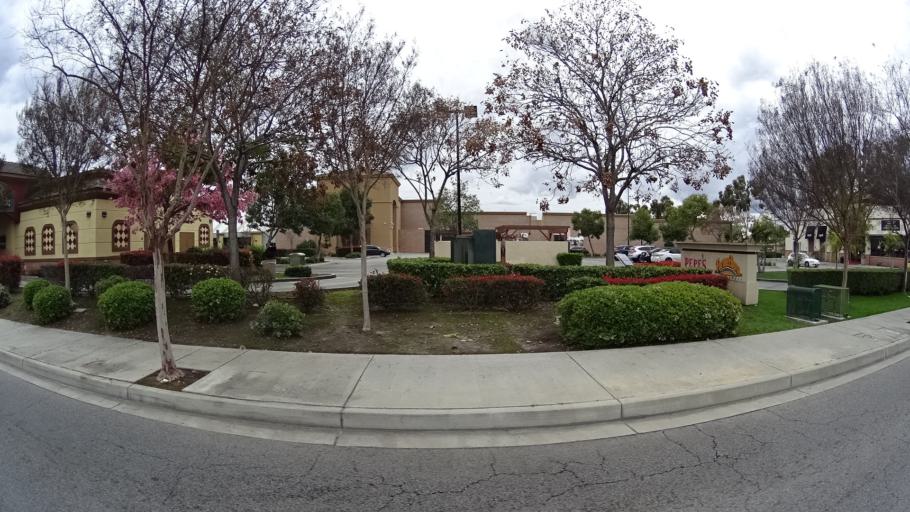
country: US
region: California
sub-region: Los Angeles County
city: Baldwin Park
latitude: 34.0731
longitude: -117.9622
